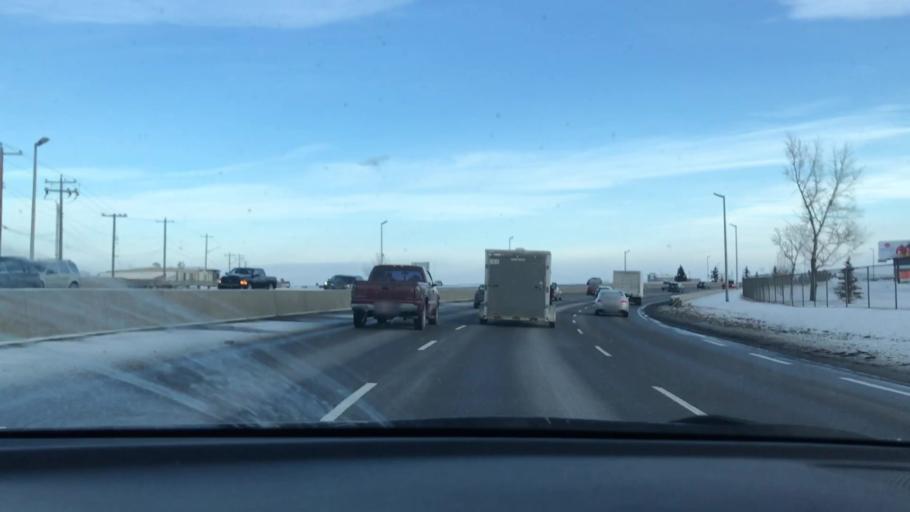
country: CA
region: Alberta
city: Calgary
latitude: 51.0960
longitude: -114.0301
